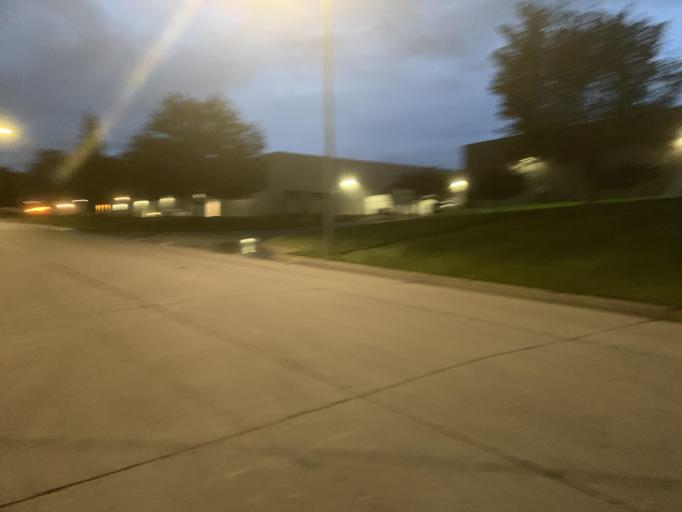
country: US
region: Nebraska
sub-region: Douglas County
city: Ralston
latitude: 41.1897
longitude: -96.0858
